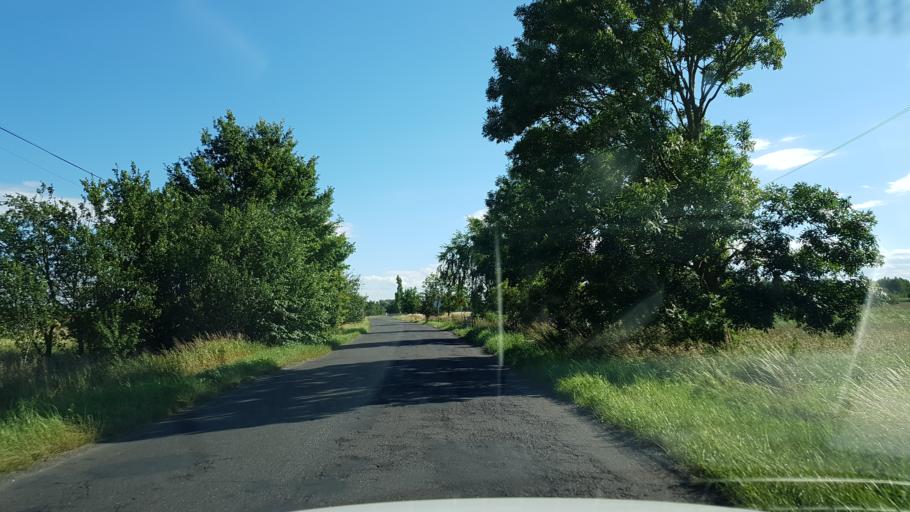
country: PL
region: West Pomeranian Voivodeship
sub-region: Powiat goleniowski
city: Stepnica
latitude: 53.6662
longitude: 14.6241
